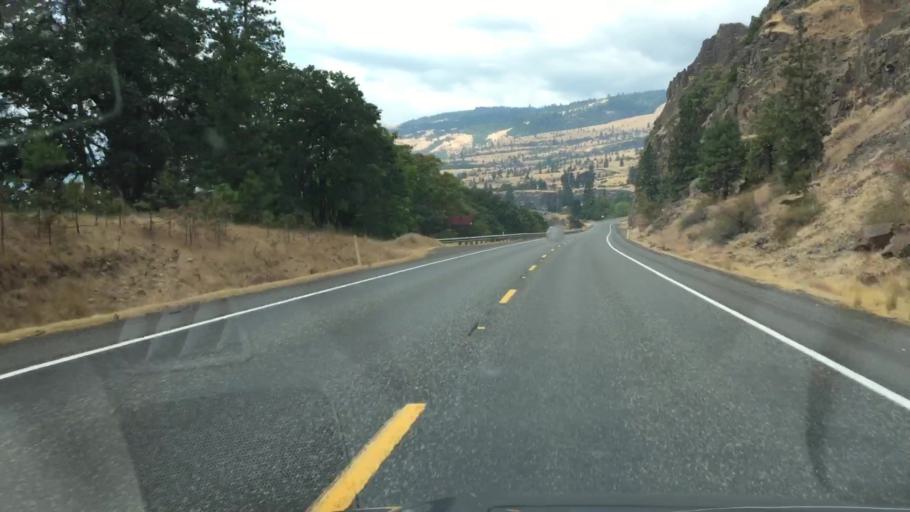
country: US
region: Oregon
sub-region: Wasco County
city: Chenoweth
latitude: 45.7081
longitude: -121.3337
